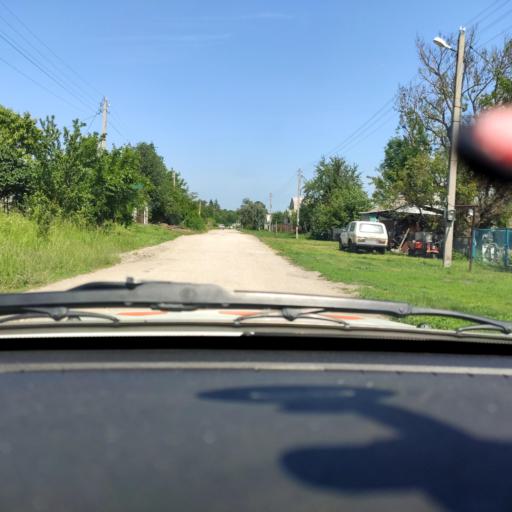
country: RU
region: Voronezj
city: Devitsa
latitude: 51.5923
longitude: 38.9915
